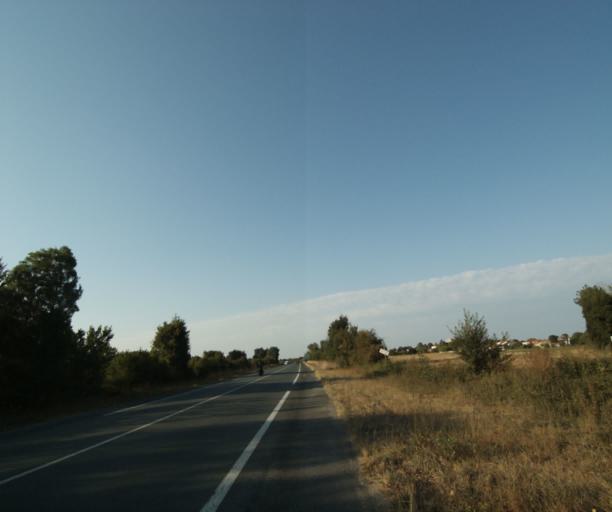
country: FR
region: Poitou-Charentes
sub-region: Departement de la Charente-Maritime
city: Saint-Hippolyte
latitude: 45.9213
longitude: -0.8843
